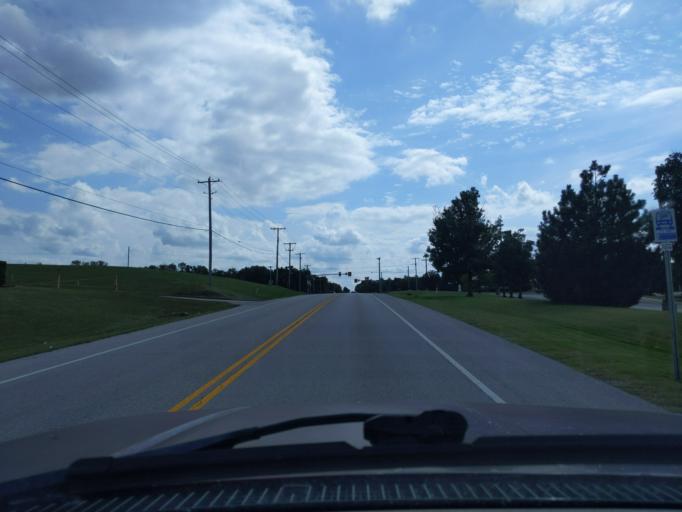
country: US
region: Oklahoma
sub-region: Tulsa County
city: Oakhurst
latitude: 36.0627
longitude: -96.0117
